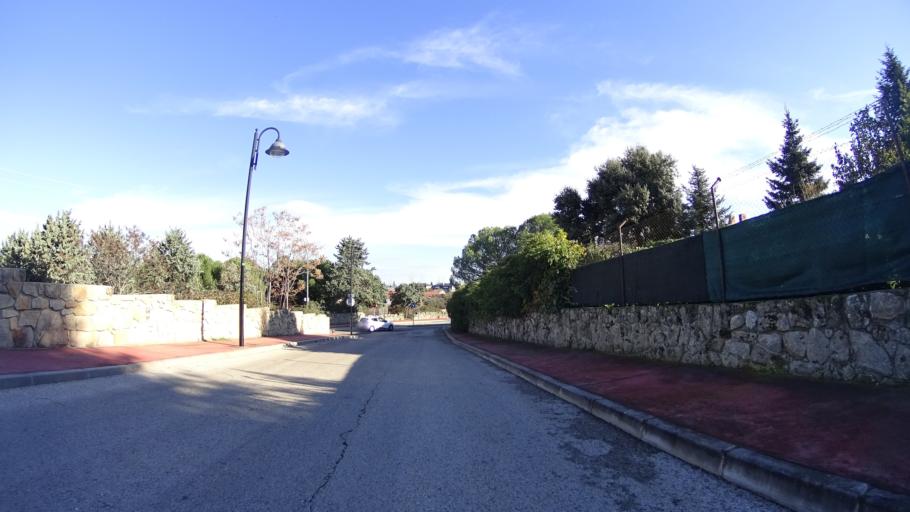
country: ES
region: Madrid
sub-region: Provincia de Madrid
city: Galapagar
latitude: 40.5722
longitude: -3.9925
